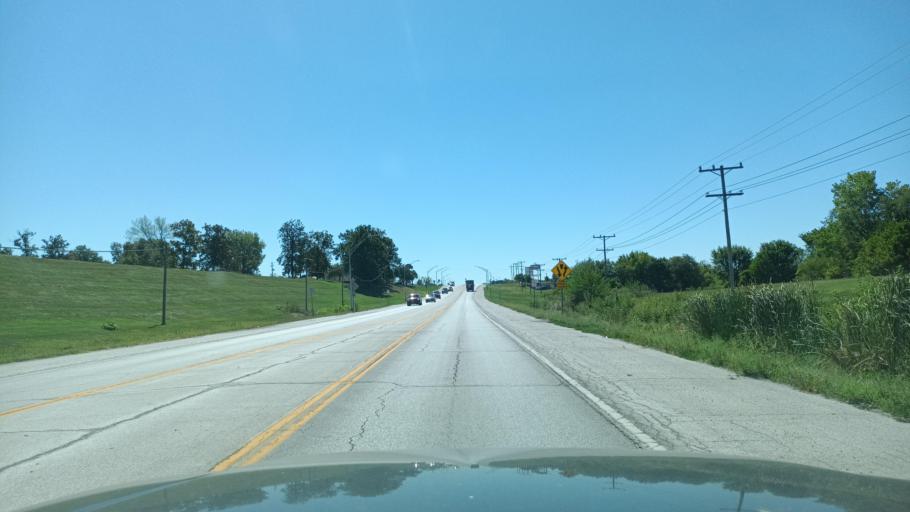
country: US
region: Missouri
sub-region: Adair County
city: Kirksville
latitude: 40.1743
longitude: -92.5720
